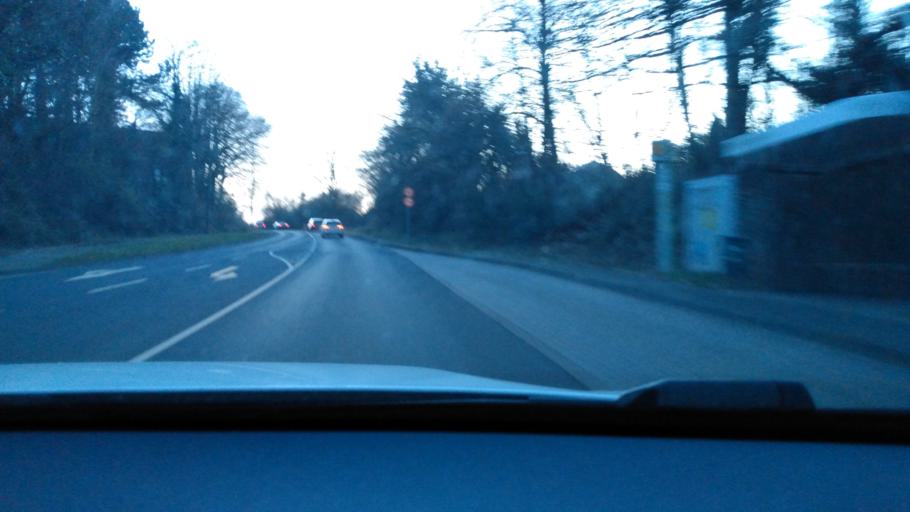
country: DE
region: North Rhine-Westphalia
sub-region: Regierungsbezirk Koln
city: Konigswinter
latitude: 50.6484
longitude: 7.1564
